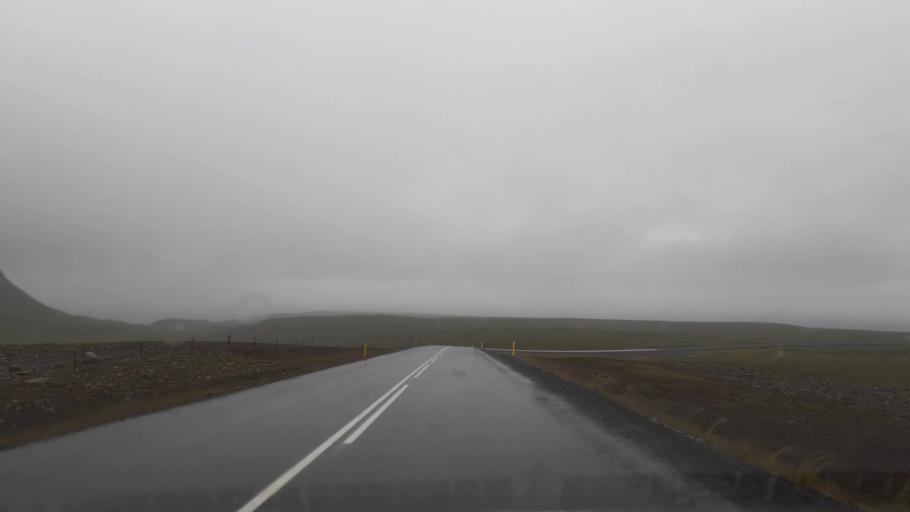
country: IS
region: Northeast
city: Husavik
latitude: 66.2366
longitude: -15.7616
